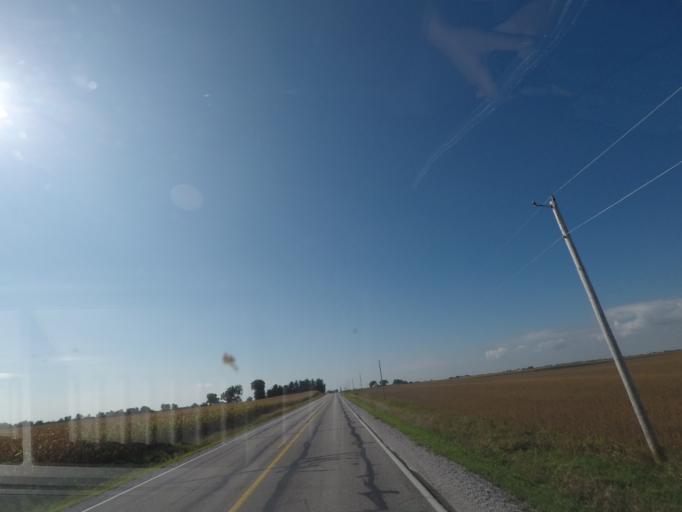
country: US
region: Iowa
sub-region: Story County
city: Nevada
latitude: 42.0298
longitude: -93.4058
